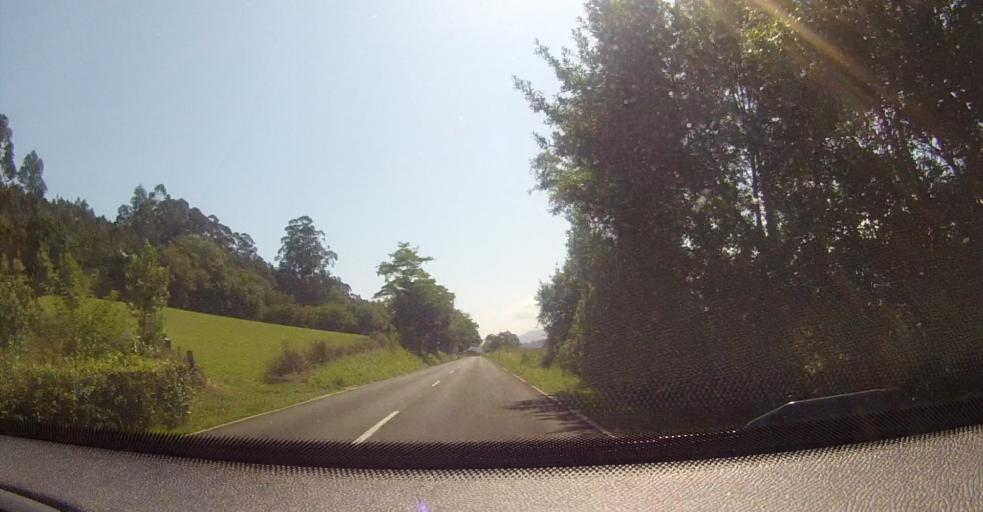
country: ES
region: Asturias
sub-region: Province of Asturias
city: Colunga
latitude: 43.4882
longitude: -5.2997
